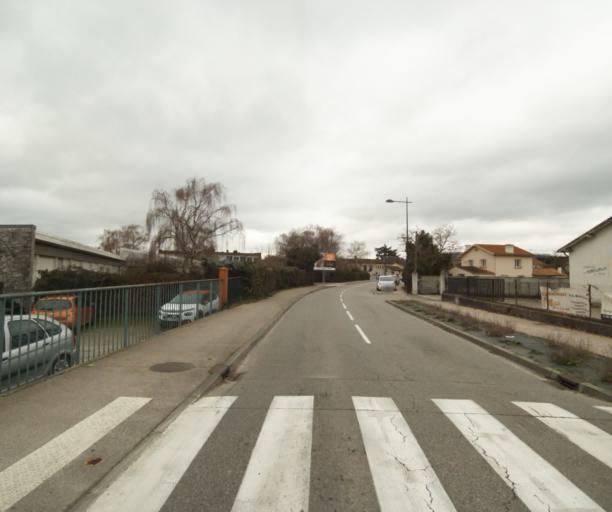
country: FR
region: Midi-Pyrenees
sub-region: Departement de l'Ariege
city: Pamiers
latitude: 43.1166
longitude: 1.6219
